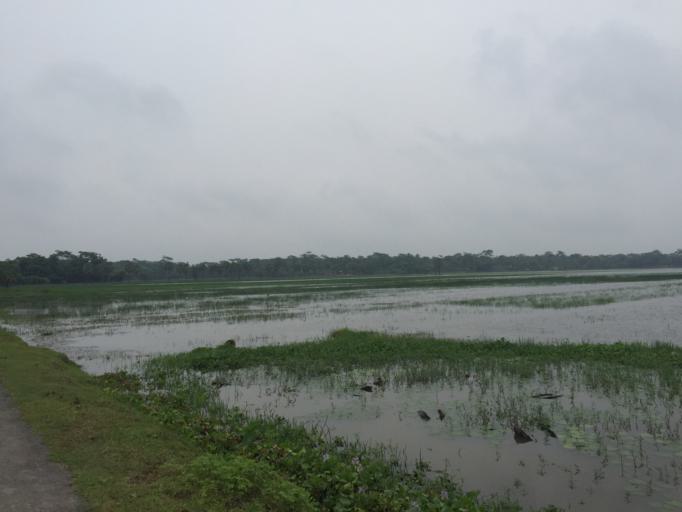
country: BD
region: Barisal
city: Mathba
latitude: 22.2113
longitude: 89.9264
